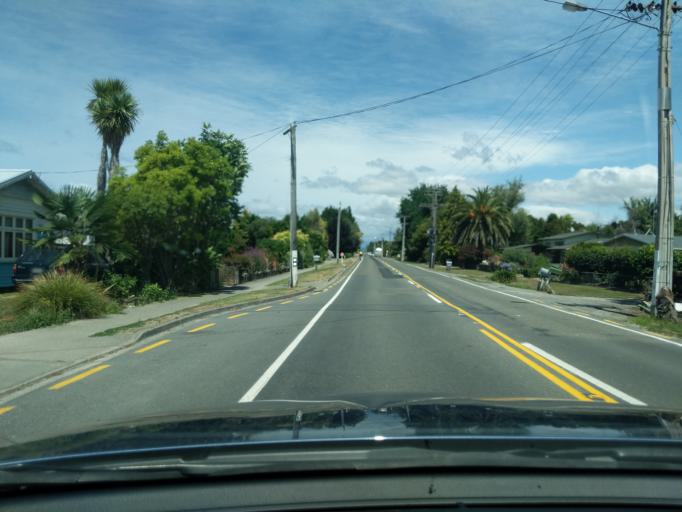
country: NZ
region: Tasman
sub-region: Tasman District
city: Motueka
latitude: -41.0768
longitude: 172.9974
